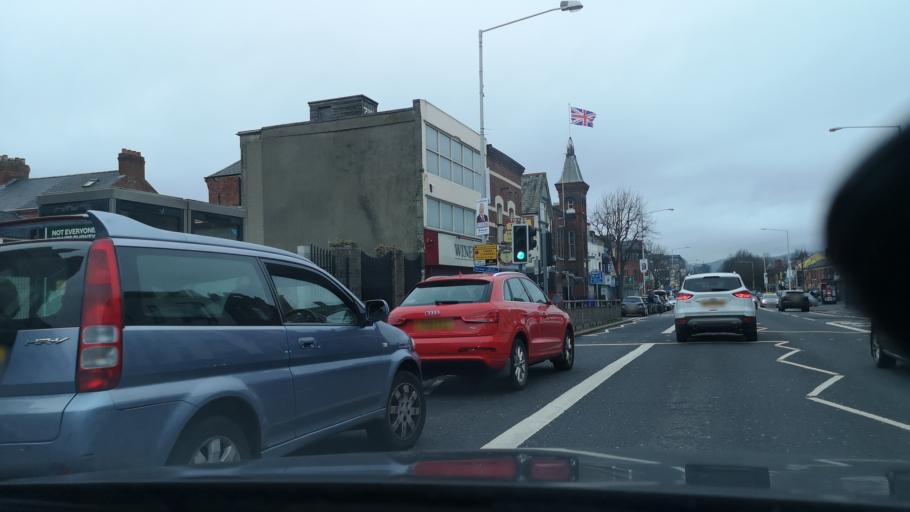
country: GB
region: Northern Ireland
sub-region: City of Belfast
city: Belfast
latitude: 54.5767
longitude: -5.9179
